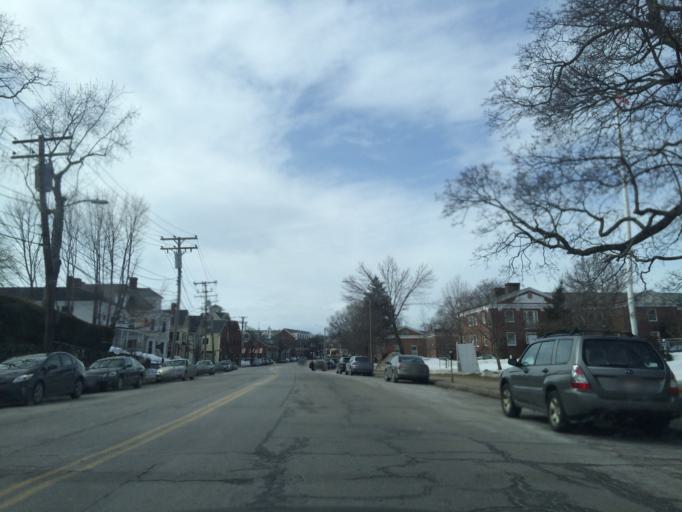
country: US
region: Massachusetts
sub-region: Middlesex County
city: Lexington
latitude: 42.4463
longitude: -71.2236
